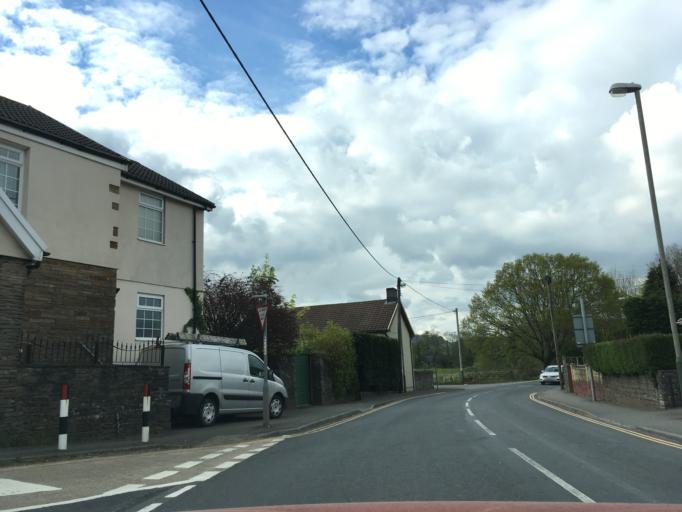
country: GB
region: Wales
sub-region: Caerphilly County Borough
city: Nelson
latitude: 51.6570
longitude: -3.2891
